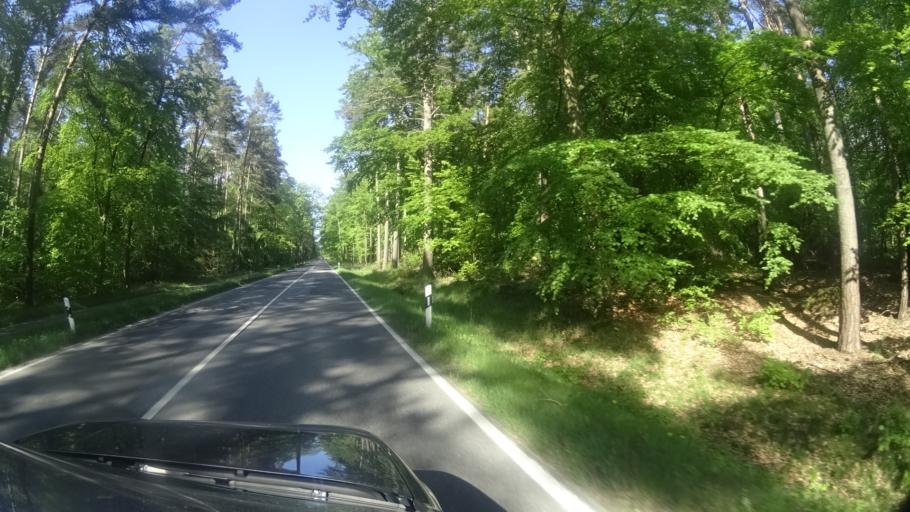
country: DE
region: Mecklenburg-Vorpommern
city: Rovershagen
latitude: 54.2161
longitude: 12.2146
